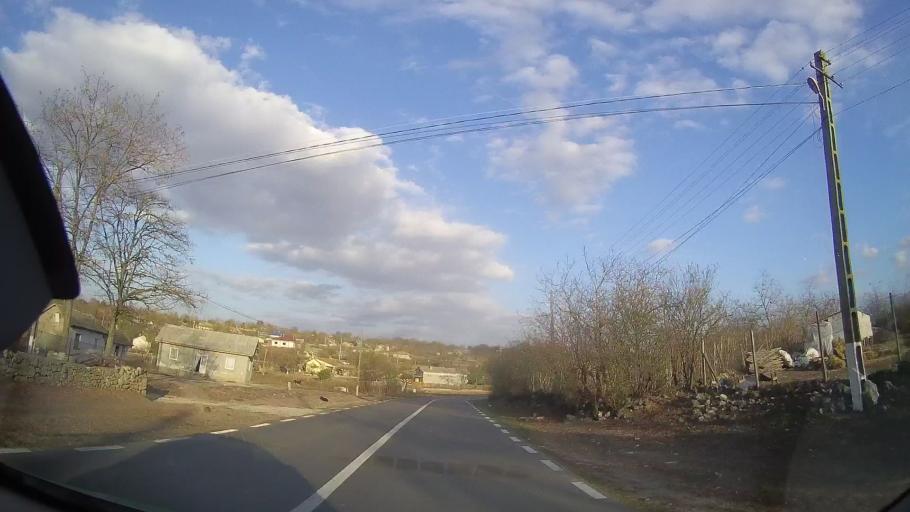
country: RO
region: Constanta
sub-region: Comuna Independenta
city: Independenta
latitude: 43.9539
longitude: 28.0756
